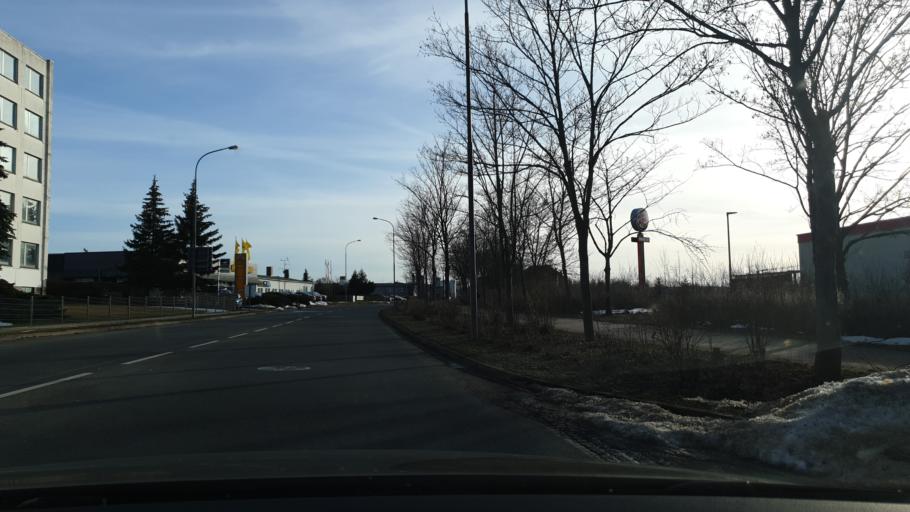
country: DE
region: Thuringia
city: Zeulenroda
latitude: 50.6608
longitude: 11.9972
